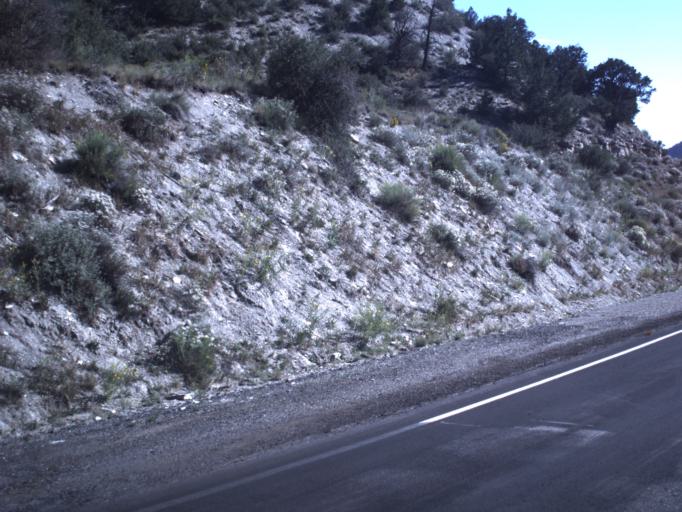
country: US
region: Utah
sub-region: Carbon County
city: Helper
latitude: 39.9152
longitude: -110.6928
